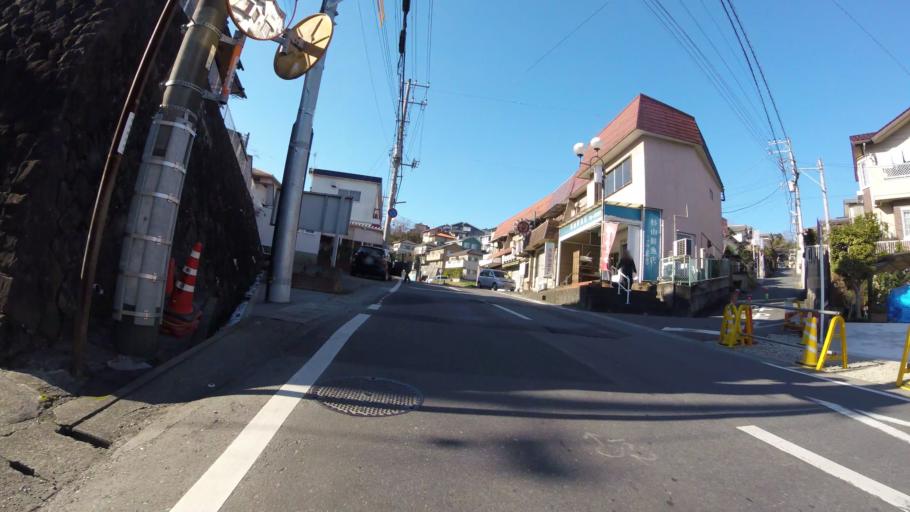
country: JP
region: Shizuoka
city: Mishima
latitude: 35.0880
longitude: 138.9650
